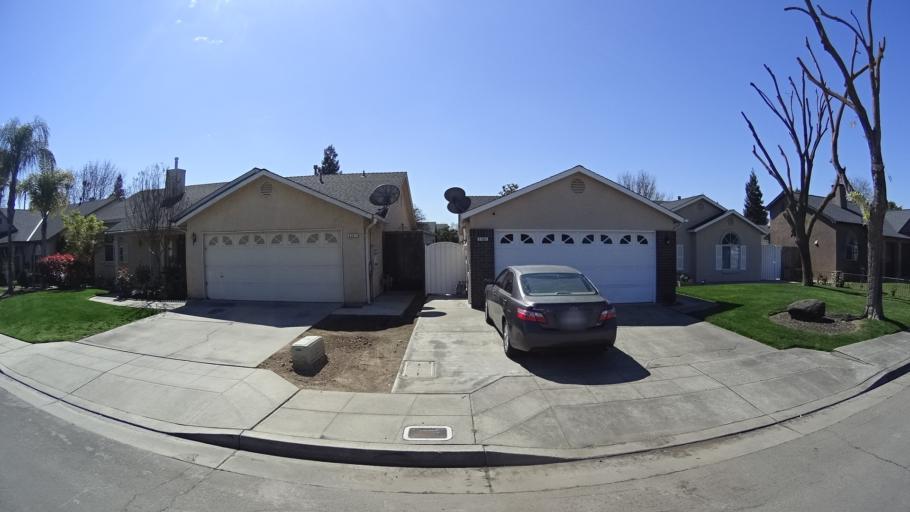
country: US
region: California
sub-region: Fresno County
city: West Park
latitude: 36.7851
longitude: -119.8869
